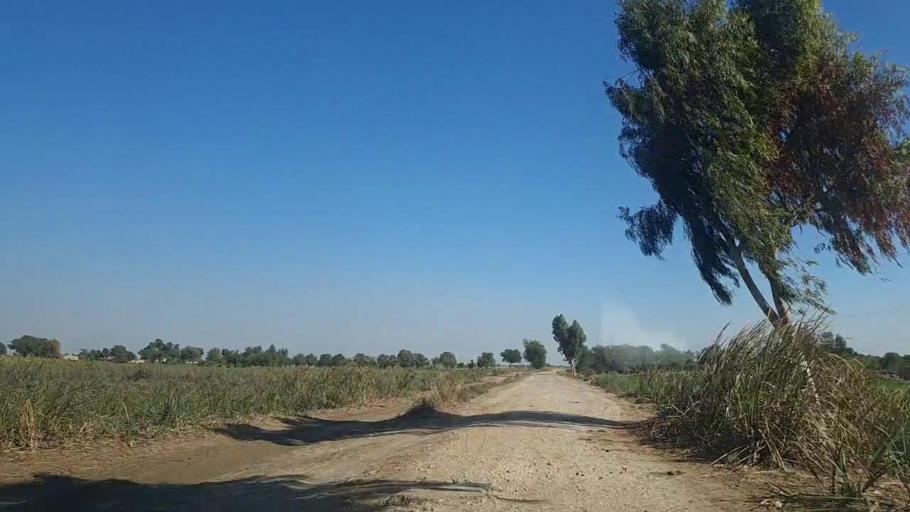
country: PK
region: Sindh
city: Sanghar
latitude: 26.2092
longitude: 68.8820
